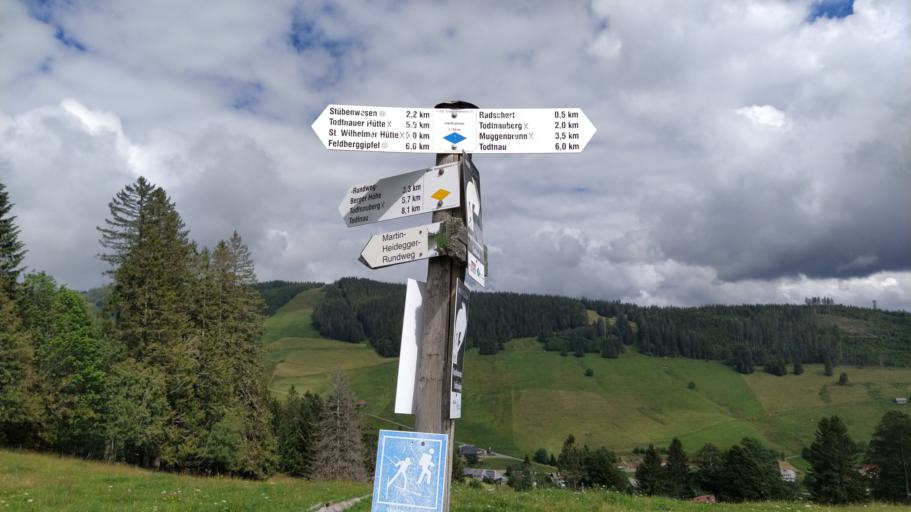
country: DE
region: Baden-Wuerttemberg
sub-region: Freiburg Region
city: Todtnau
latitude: 47.8607
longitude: 7.9446
